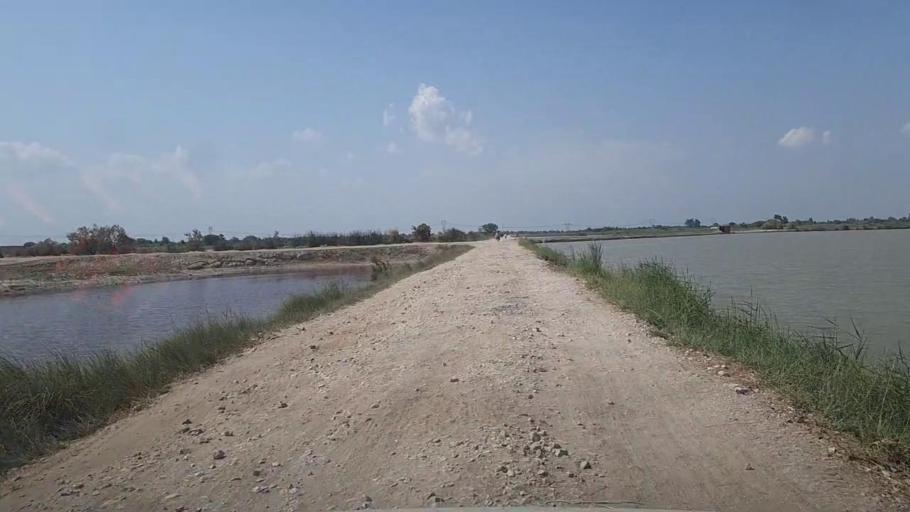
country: PK
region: Sindh
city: Khairpur
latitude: 28.0970
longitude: 69.6276
